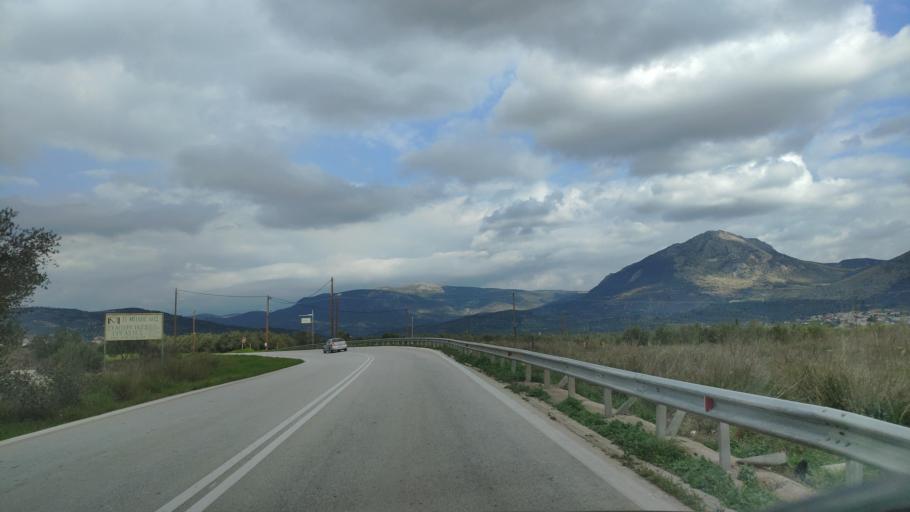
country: GR
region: Peloponnese
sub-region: Nomos Argolidos
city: Koutsopodi
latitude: 37.7104
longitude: 22.7257
